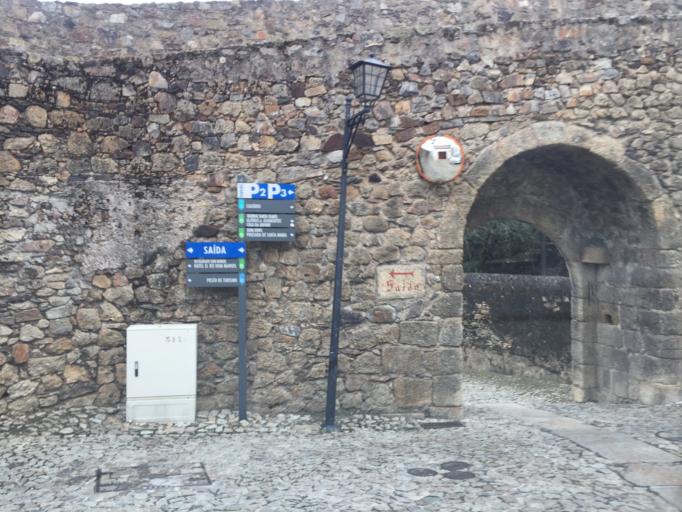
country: PT
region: Portalegre
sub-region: Marvao
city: Marvao
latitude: 39.3937
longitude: -7.3751
